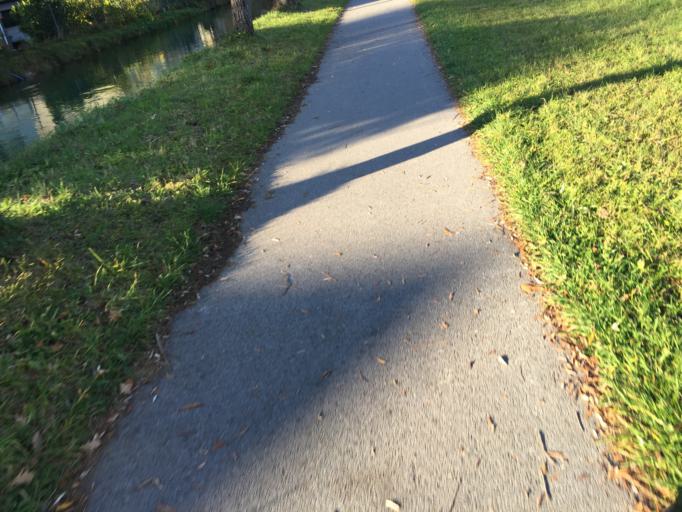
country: AT
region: Salzburg
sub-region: Politischer Bezirk Salzburg-Umgebung
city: Anif
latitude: 47.7668
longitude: 13.0394
